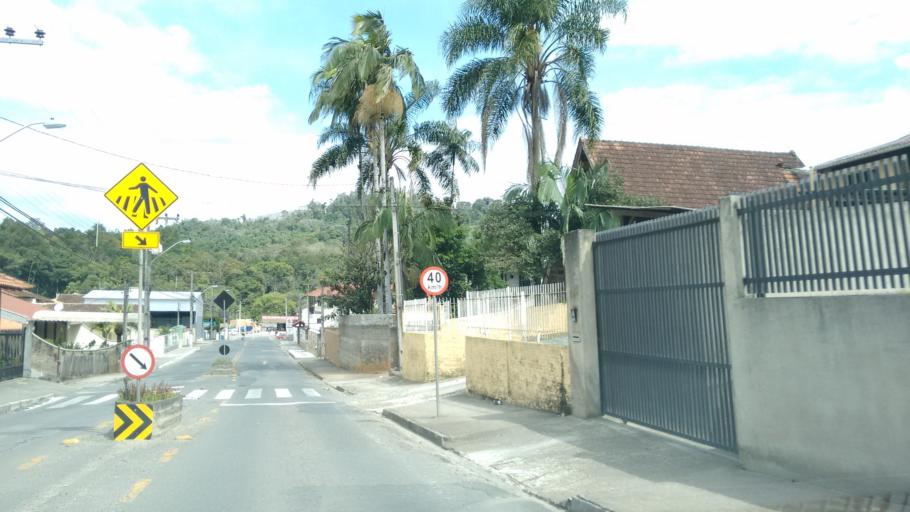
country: BR
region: Santa Catarina
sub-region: Blumenau
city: Blumenau
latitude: -26.8621
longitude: -49.1262
